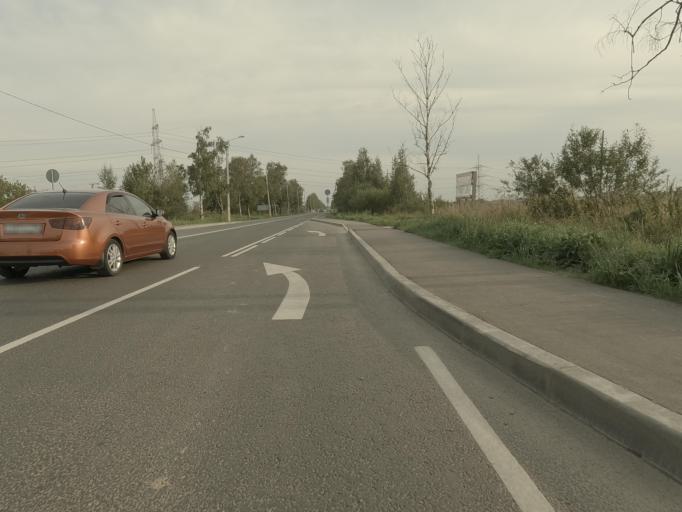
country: RU
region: St.-Petersburg
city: Strel'na
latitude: 59.8506
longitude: 30.0905
